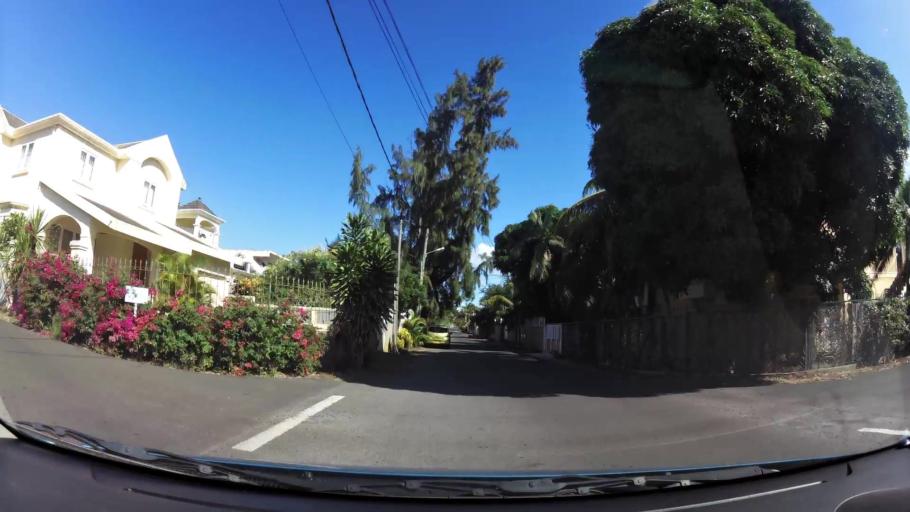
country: MU
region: Black River
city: Albion
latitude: -20.2150
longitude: 57.4057
